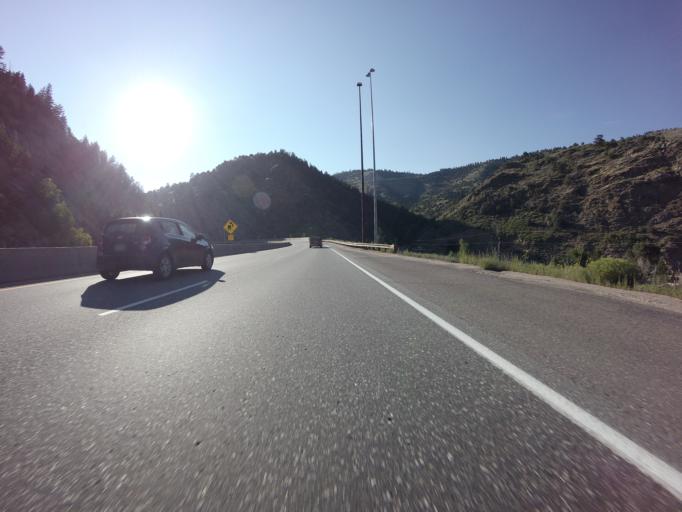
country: US
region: Colorado
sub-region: Clear Creek County
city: Idaho Springs
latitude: 39.7453
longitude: -105.4367
